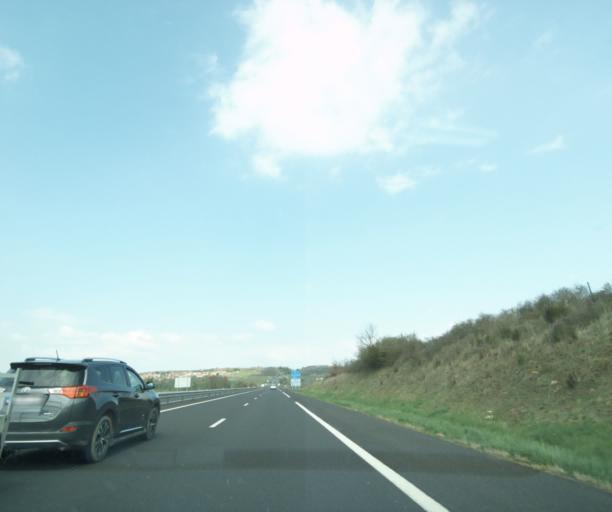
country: FR
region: Auvergne
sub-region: Departement de la Haute-Loire
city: Bournoncle-Saint-Pierre
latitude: 45.3206
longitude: 3.2616
